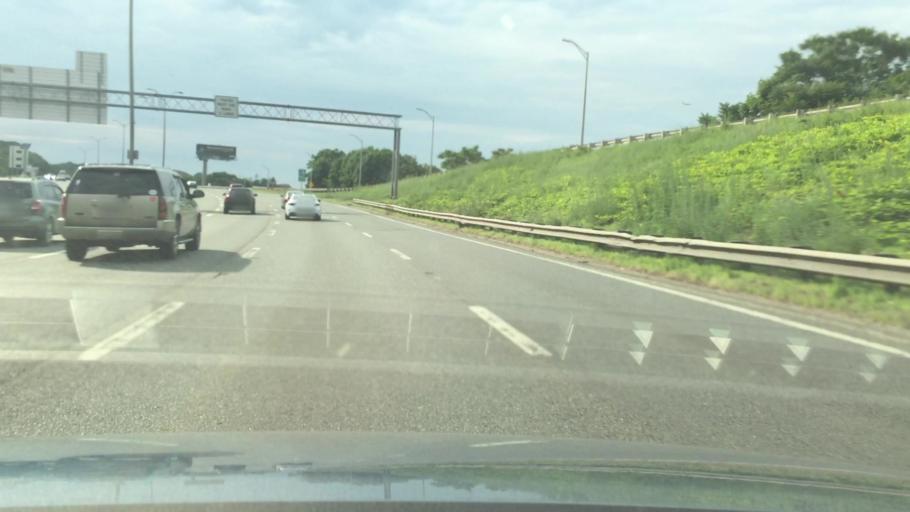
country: US
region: Massachusetts
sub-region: Norfolk County
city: Quincy
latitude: 42.2433
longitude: -71.0280
